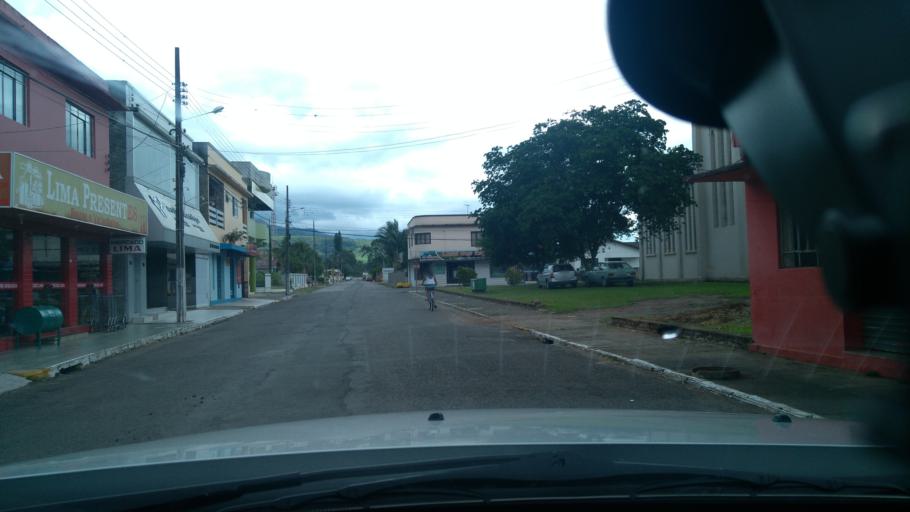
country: BR
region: Rio Grande do Sul
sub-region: Torres
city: Torres
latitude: -29.1973
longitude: -49.9510
